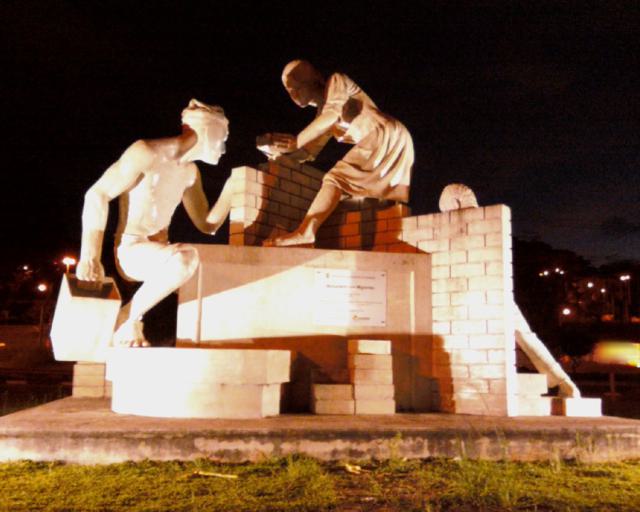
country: BR
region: Sao Paulo
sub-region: Diadema
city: Diadema
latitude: -23.6846
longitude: -46.6120
